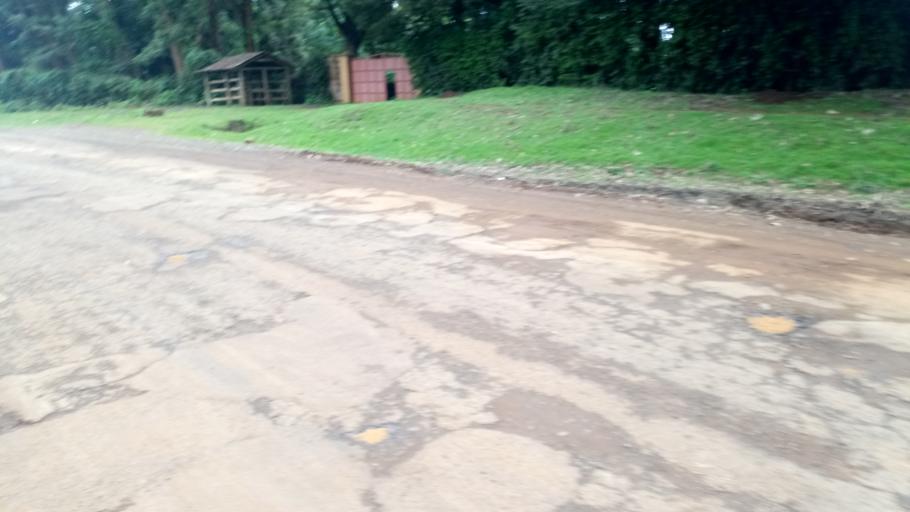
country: KE
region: Kirinyaga
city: Keruguya
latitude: -0.4220
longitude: 37.1587
